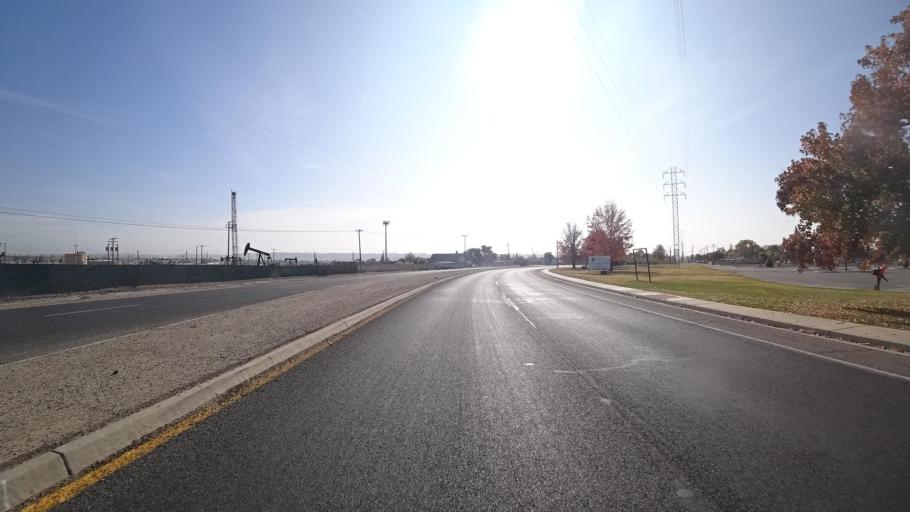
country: US
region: California
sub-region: Kern County
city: Oildale
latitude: 35.4374
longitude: -119.0132
